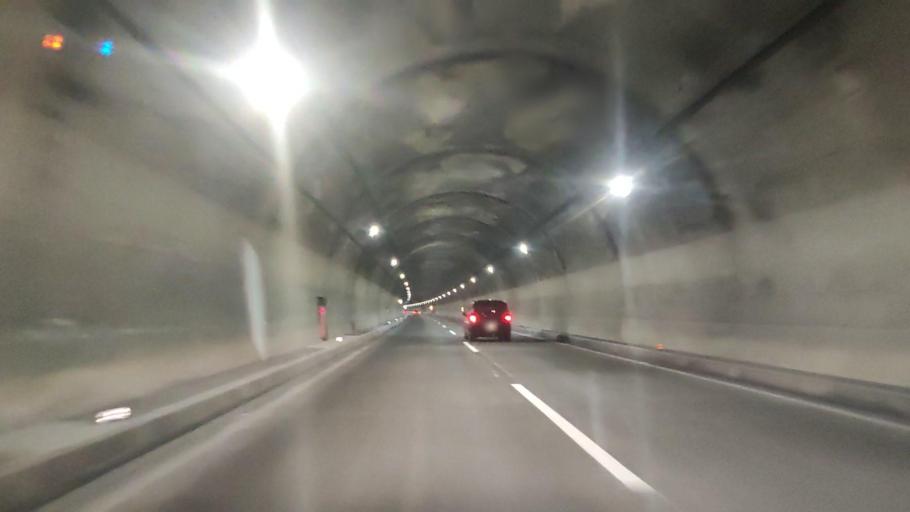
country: JP
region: Oita
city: Beppu
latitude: 33.2712
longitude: 131.3416
